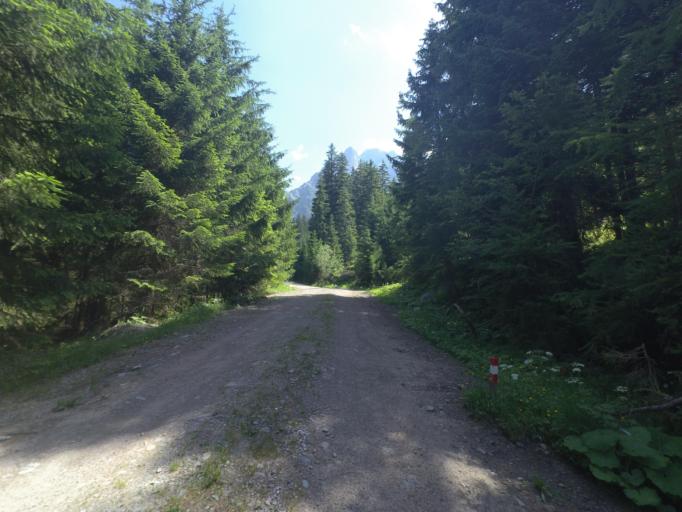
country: AT
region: Salzburg
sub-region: Politischer Bezirk Zell am See
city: Dienten am Hochkonig
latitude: 47.4195
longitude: 12.9976
